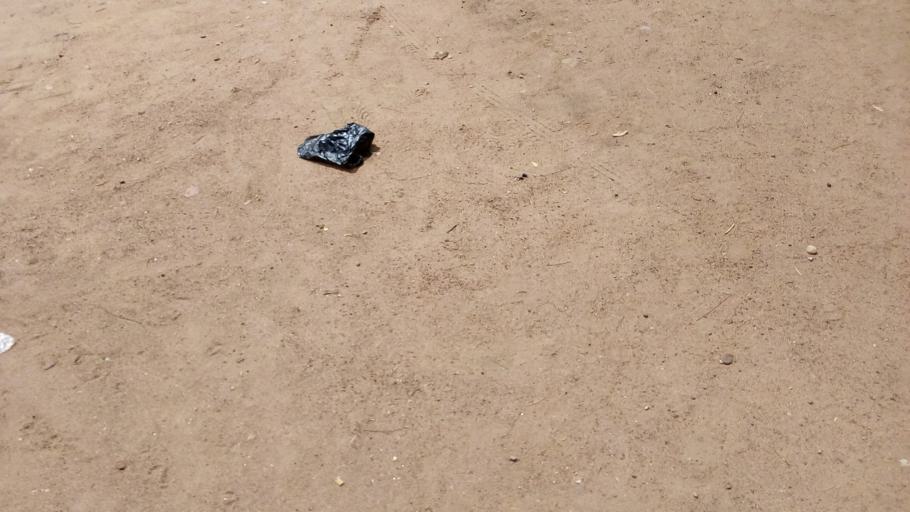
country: CI
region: Vallee du Bandama
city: Bouake
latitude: 7.6929
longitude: -5.0199
